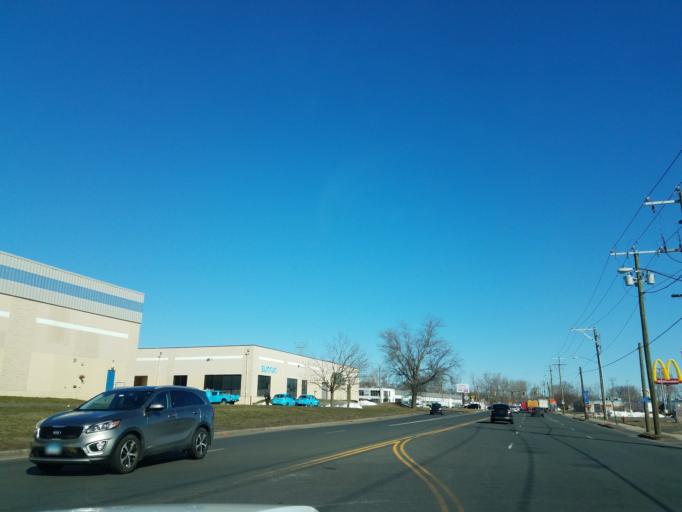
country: US
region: Connecticut
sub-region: Hartford County
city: Wethersfield
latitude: 41.7375
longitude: -72.6598
